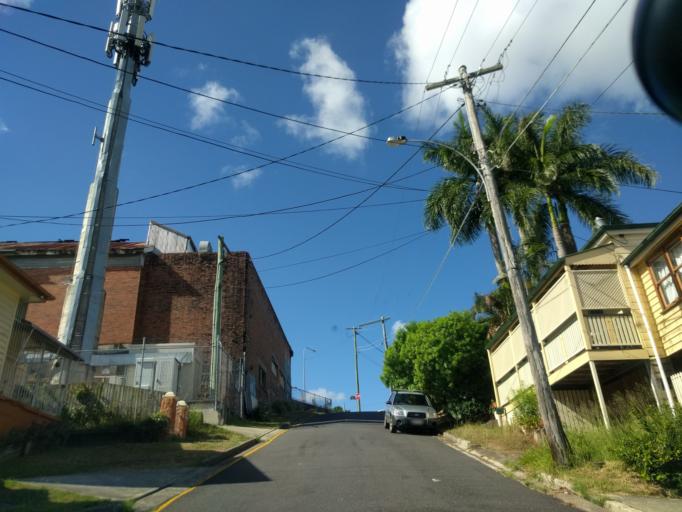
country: AU
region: Queensland
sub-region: Brisbane
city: Milton
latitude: -27.4534
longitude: 153.0046
